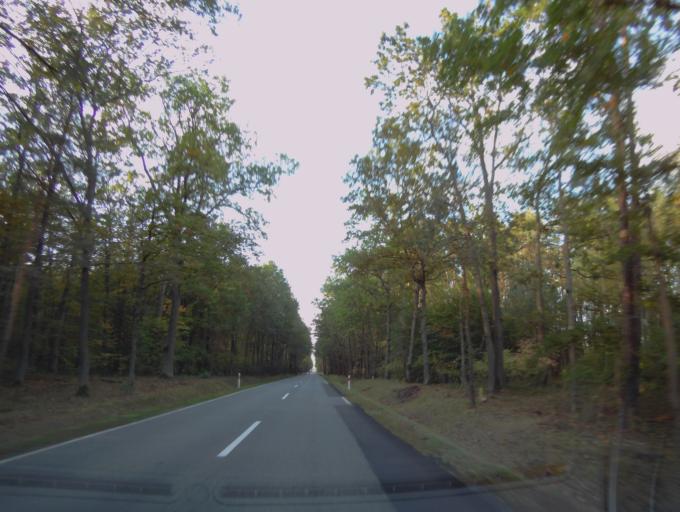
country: PL
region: Subcarpathian Voivodeship
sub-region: Powiat nizanski
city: Krzeszow
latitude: 50.3915
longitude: 22.3027
